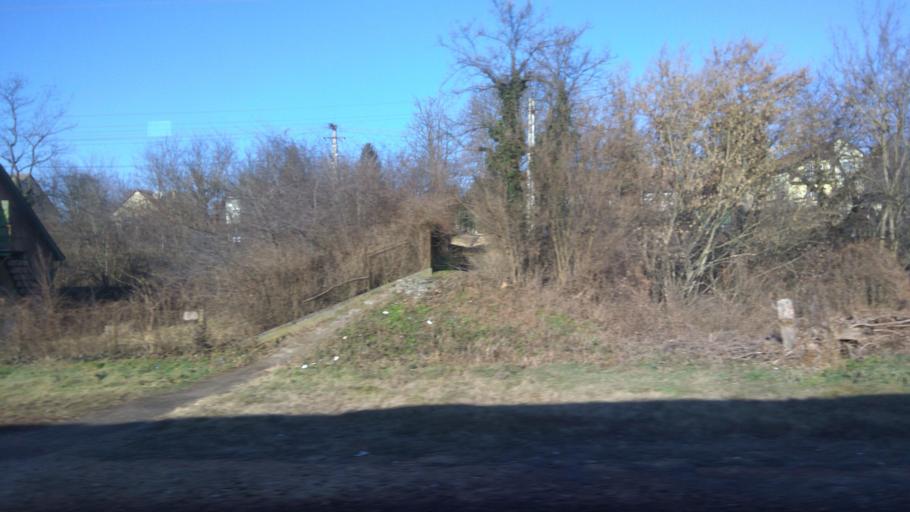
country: HU
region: Pest
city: Pecel
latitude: 47.4937
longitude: 19.3422
